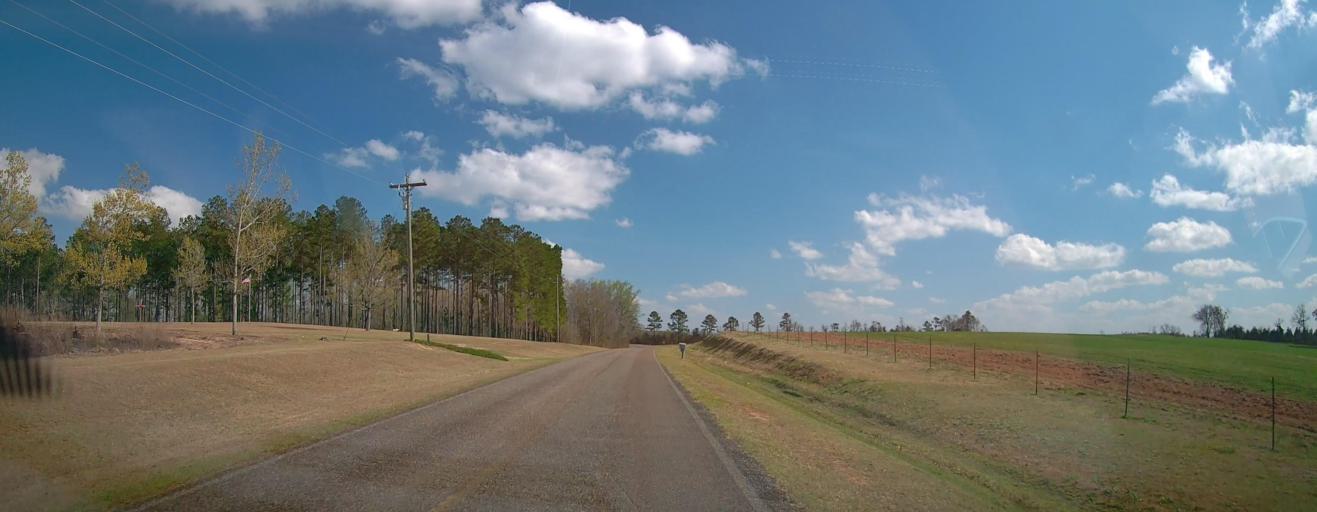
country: US
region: Georgia
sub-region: Twiggs County
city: Jeffersonville
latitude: 32.6521
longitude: -83.2026
